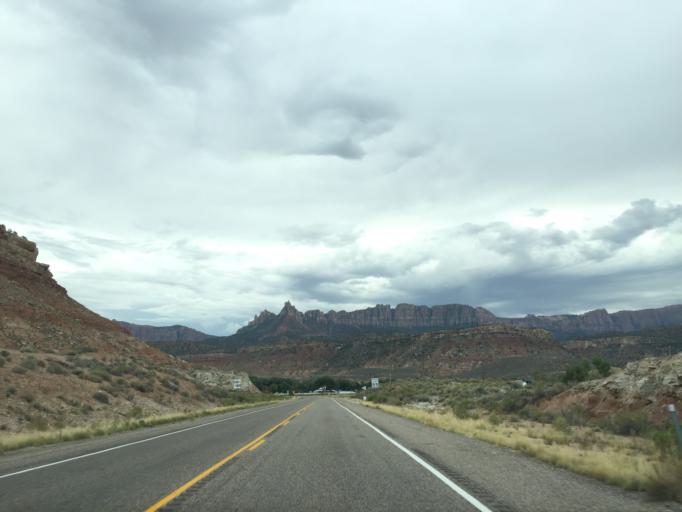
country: US
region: Utah
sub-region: Washington County
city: Hildale
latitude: 37.1660
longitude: -113.0626
